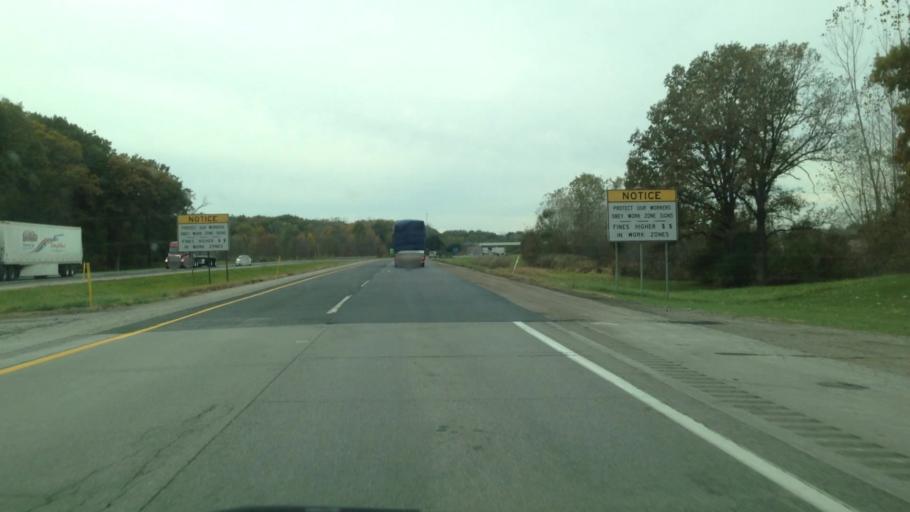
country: US
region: Indiana
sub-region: Steuben County
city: Hamilton
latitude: 41.6287
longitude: -84.8056
